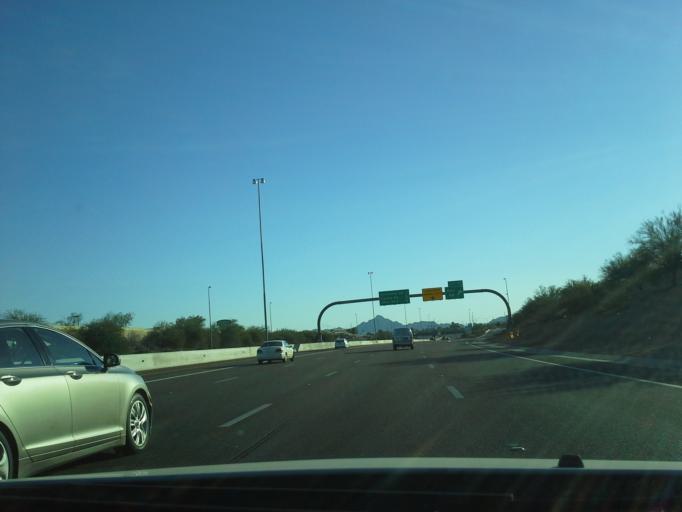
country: US
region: Arizona
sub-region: Maricopa County
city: Paradise Valley
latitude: 33.6462
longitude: -112.0013
